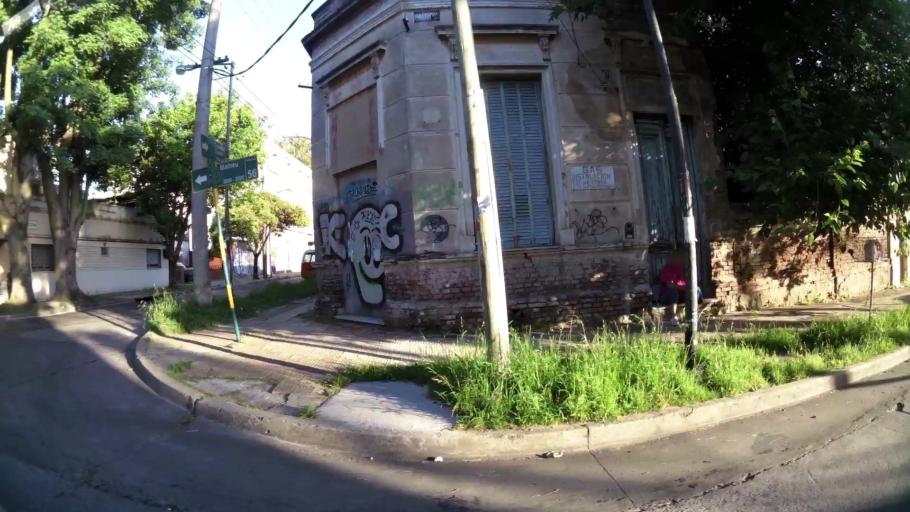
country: AR
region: Buenos Aires
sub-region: Partido de General San Martin
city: General San Martin
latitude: -34.5697
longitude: -58.5320
